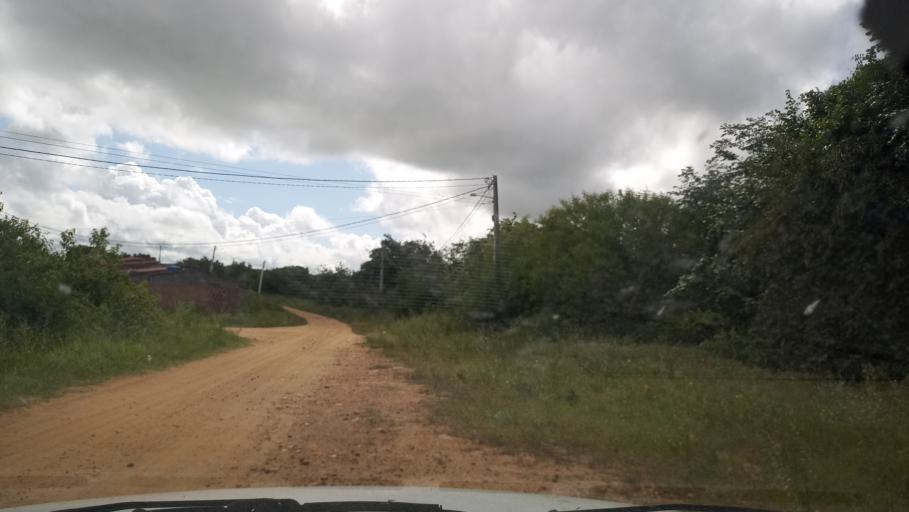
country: BR
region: Rio Grande do Norte
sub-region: Brejinho
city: Brejinho
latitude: -6.1479
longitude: -35.4308
